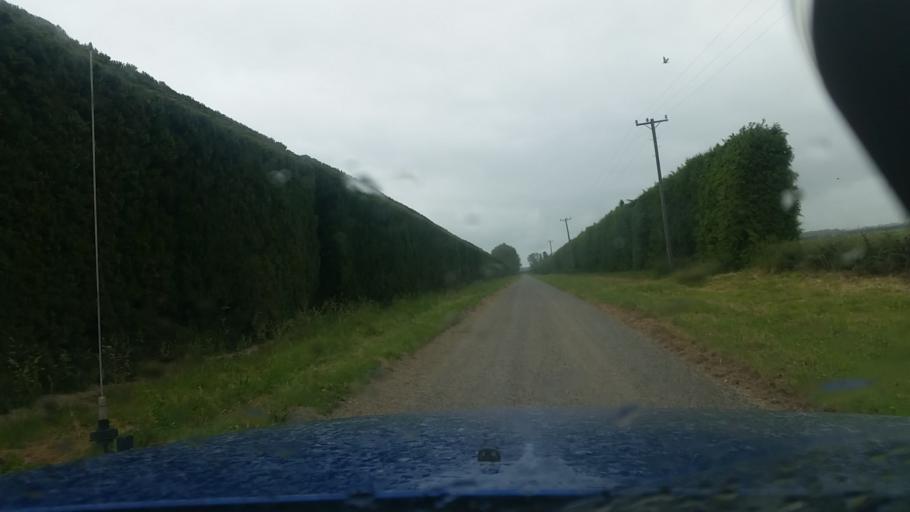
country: NZ
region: Canterbury
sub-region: Ashburton District
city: Ashburton
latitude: -43.7777
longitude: 171.7001
